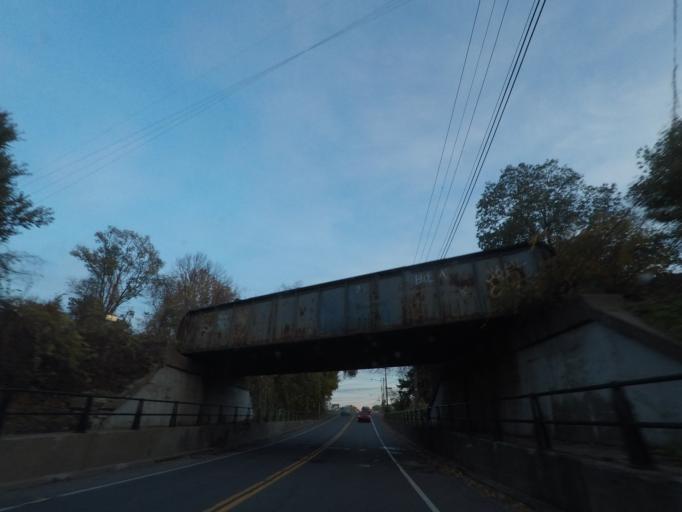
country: US
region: New York
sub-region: Schenectady County
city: Rotterdam
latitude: 42.7825
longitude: -73.9610
